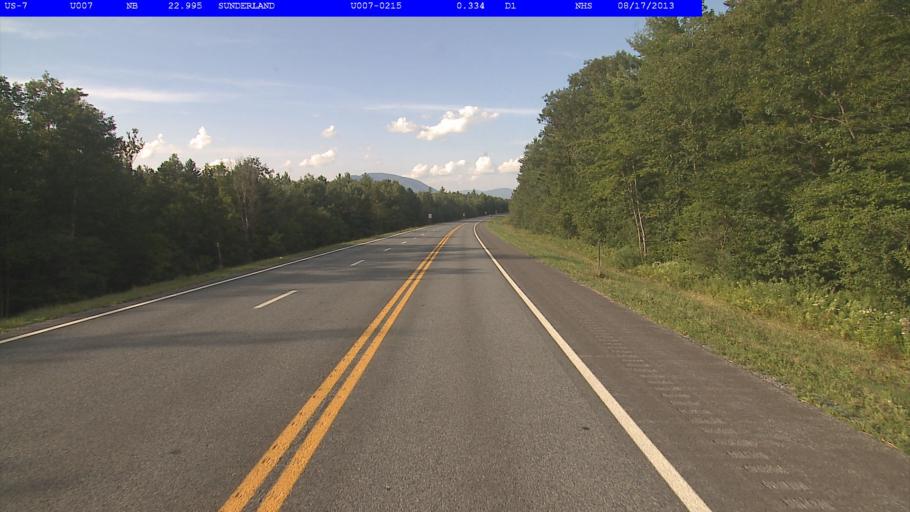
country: US
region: Vermont
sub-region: Bennington County
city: Arlington
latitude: 43.0305
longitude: -73.1388
